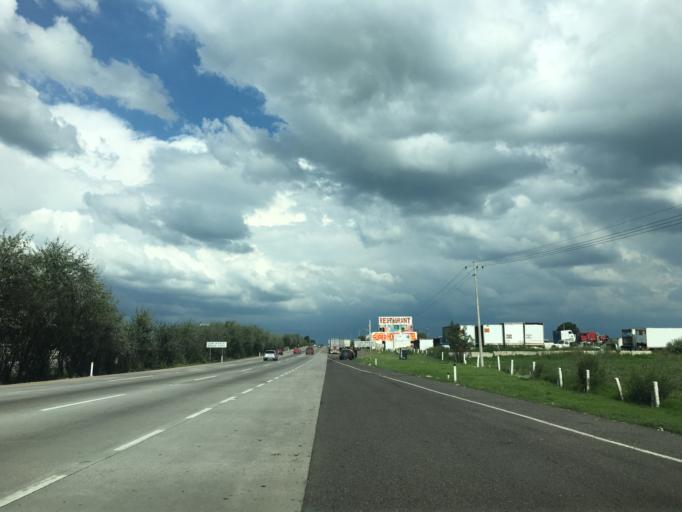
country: MX
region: Mexico
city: San Francisco Soyaniquilpan
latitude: 19.9960
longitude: -99.4833
